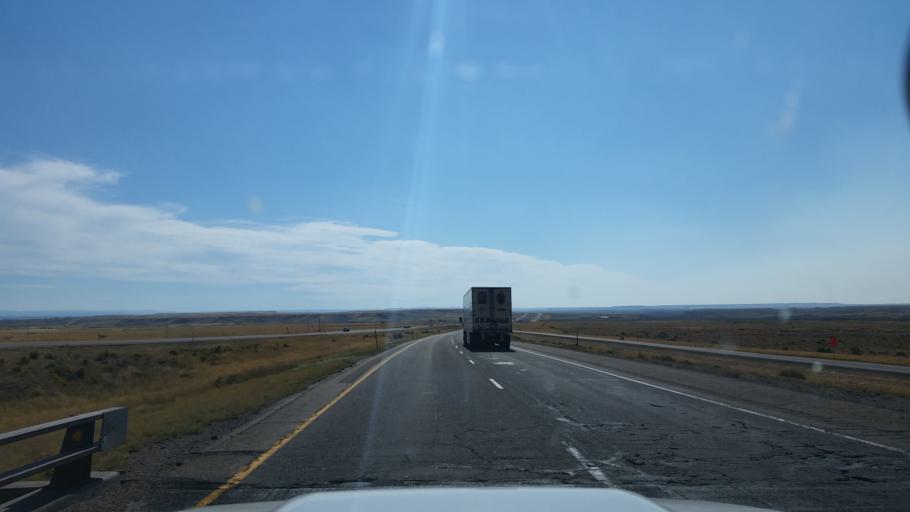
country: US
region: Wyoming
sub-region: Uinta County
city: Lyman
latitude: 41.3929
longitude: -110.1849
